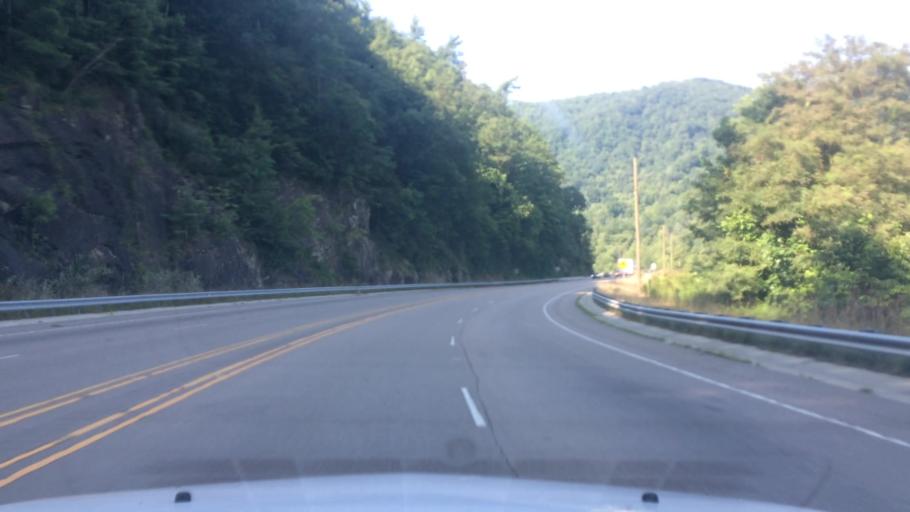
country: US
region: North Carolina
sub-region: Watauga County
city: Blowing Rock
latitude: 36.0434
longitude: -81.5931
